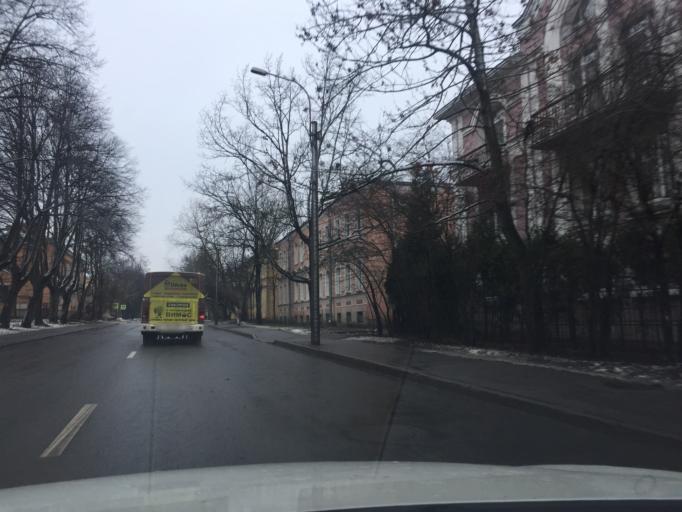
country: RU
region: St.-Petersburg
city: Pushkin
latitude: 59.7161
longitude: 30.4068
